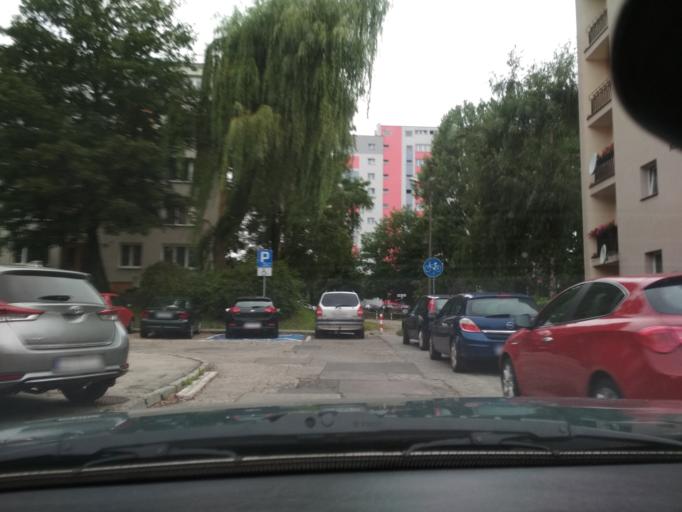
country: PL
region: Silesian Voivodeship
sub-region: Gliwice
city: Gliwice
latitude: 50.2755
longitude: 18.6538
